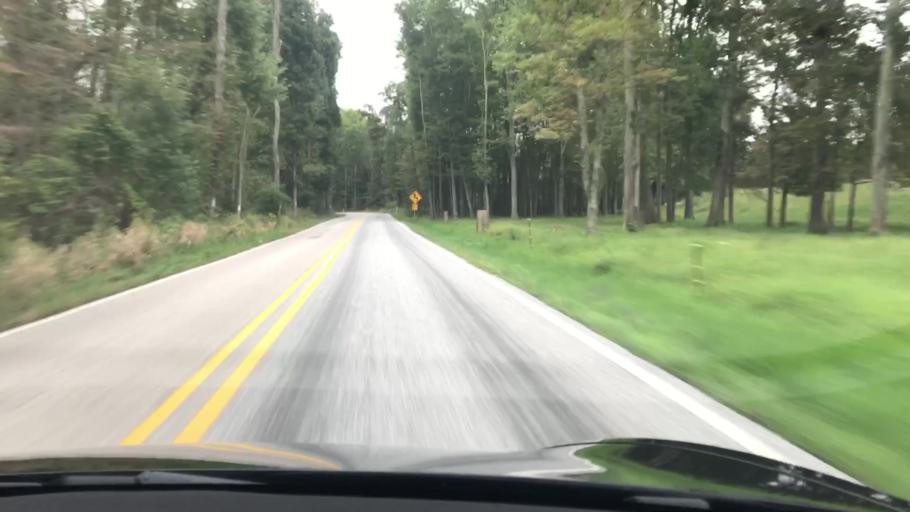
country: US
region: Pennsylvania
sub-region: York County
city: Dillsburg
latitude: 40.0604
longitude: -77.0752
